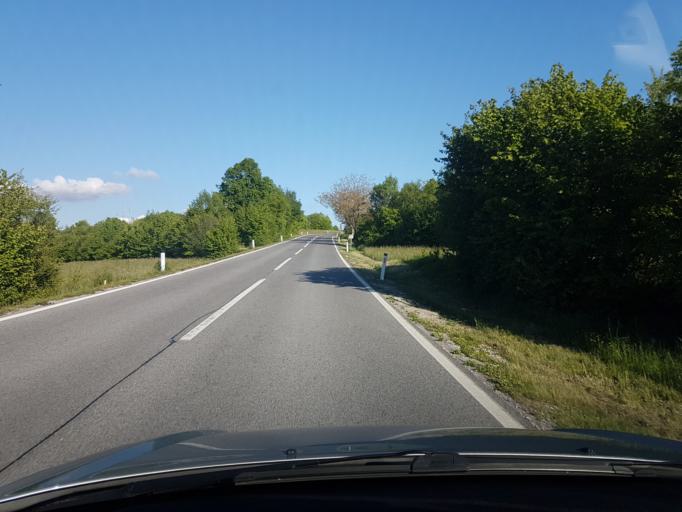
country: SI
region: Divaca
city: Divaca
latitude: 45.6954
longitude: 13.9497
